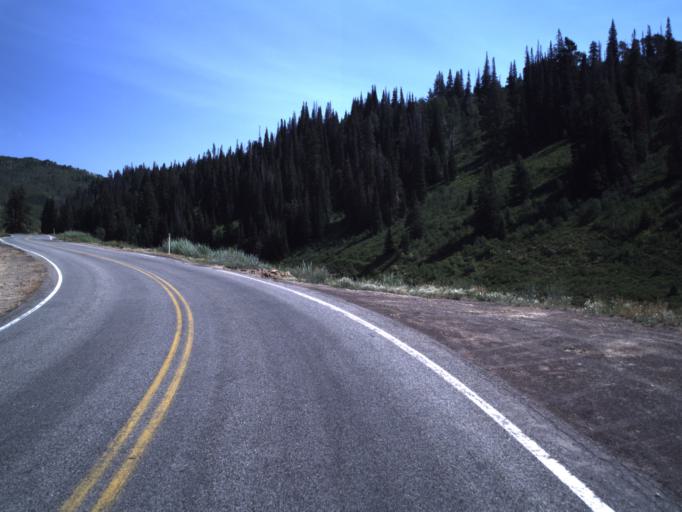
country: US
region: Utah
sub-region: Sanpete County
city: Fairview
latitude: 39.6692
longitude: -111.3409
